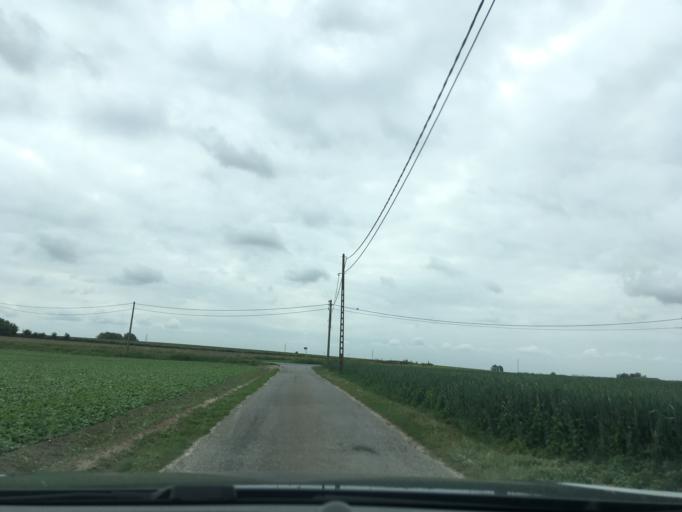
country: BE
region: Flanders
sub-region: Provincie West-Vlaanderen
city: Ledegem
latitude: 50.8420
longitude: 3.0750
